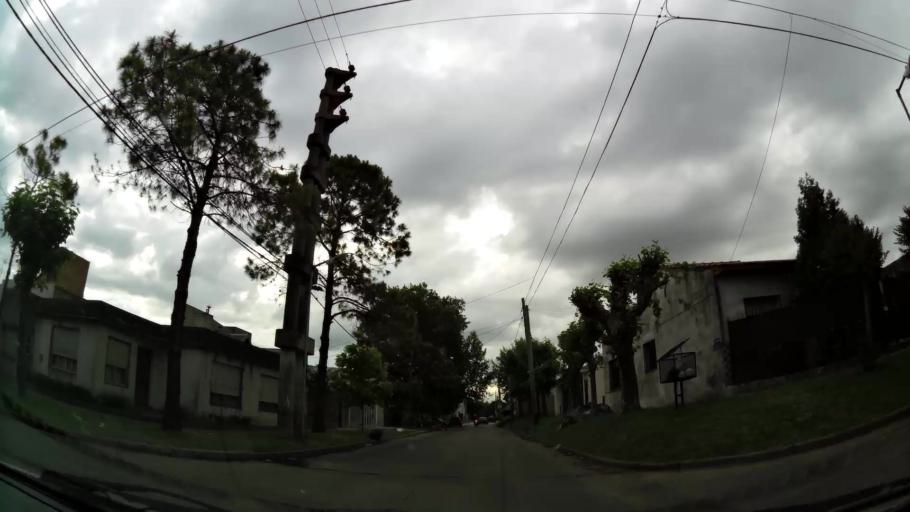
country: AR
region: Buenos Aires
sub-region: Partido de Quilmes
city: Quilmes
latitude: -34.7422
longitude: -58.2414
